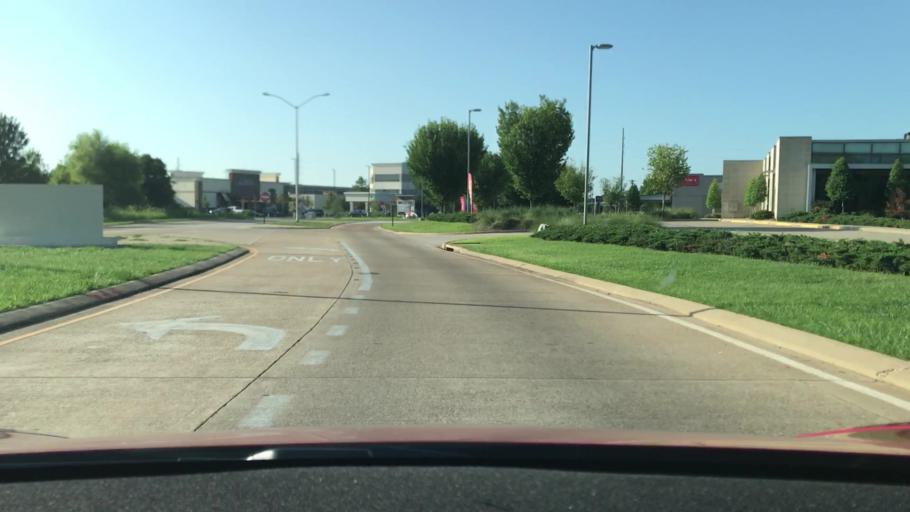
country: US
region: Louisiana
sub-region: Bossier Parish
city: Bossier City
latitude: 32.4461
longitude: -93.7307
